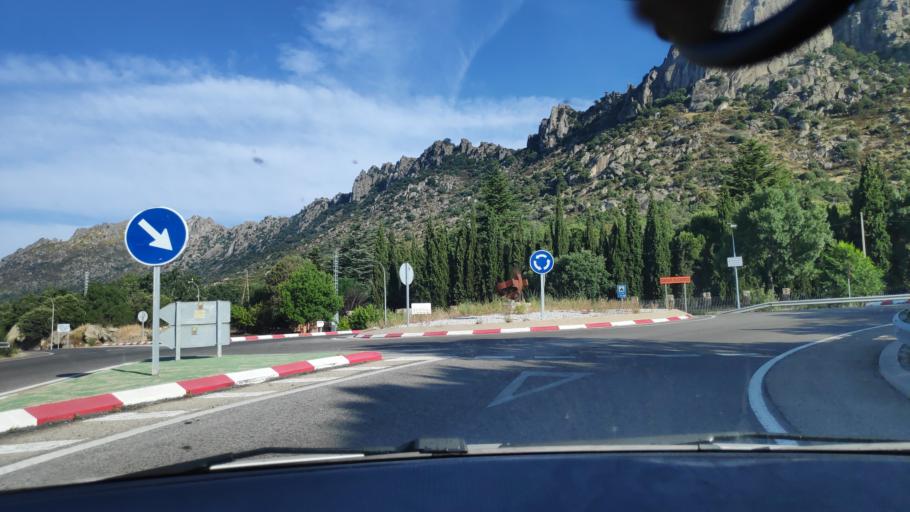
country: ES
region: Madrid
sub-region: Provincia de Madrid
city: La Cabrera
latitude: 40.8744
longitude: -3.6037
